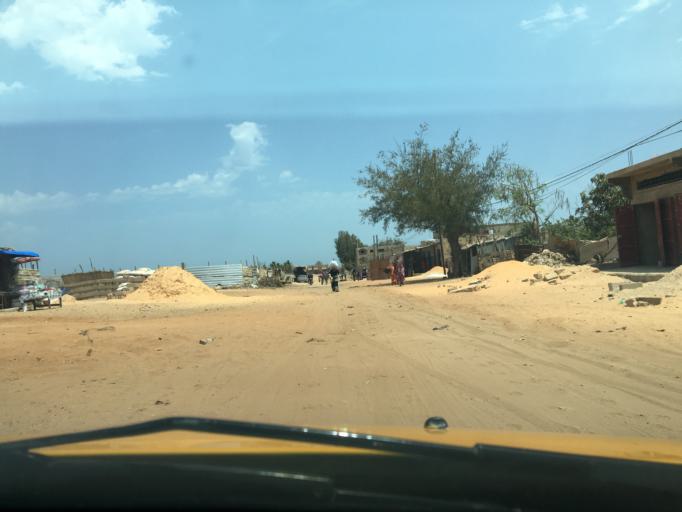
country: SN
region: Thies
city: Thies
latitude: 14.8039
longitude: -17.1857
